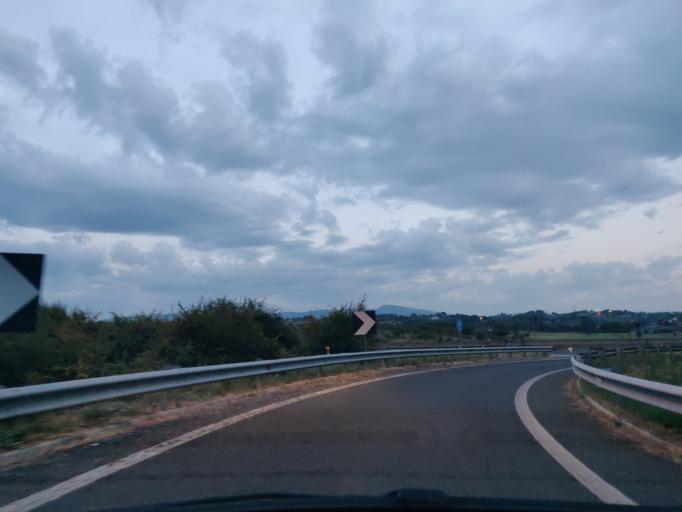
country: IT
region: Latium
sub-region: Provincia di Viterbo
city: Vetralla
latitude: 42.3762
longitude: 12.0525
